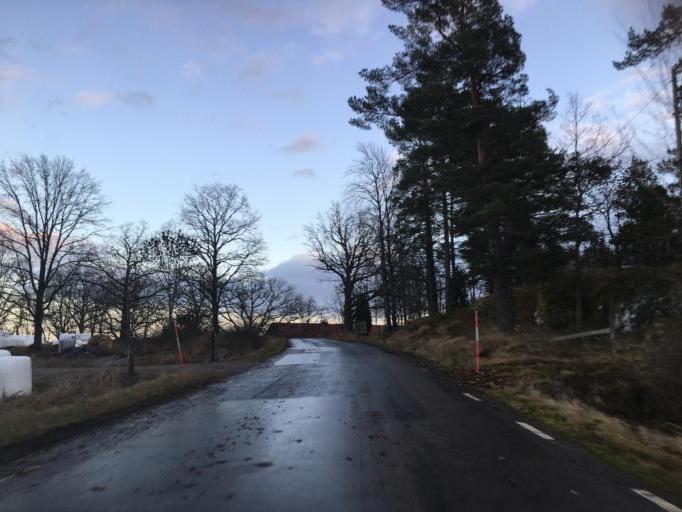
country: SE
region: Kalmar
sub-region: Vasterviks Kommun
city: Vaestervik
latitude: 57.5900
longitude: 16.5052
